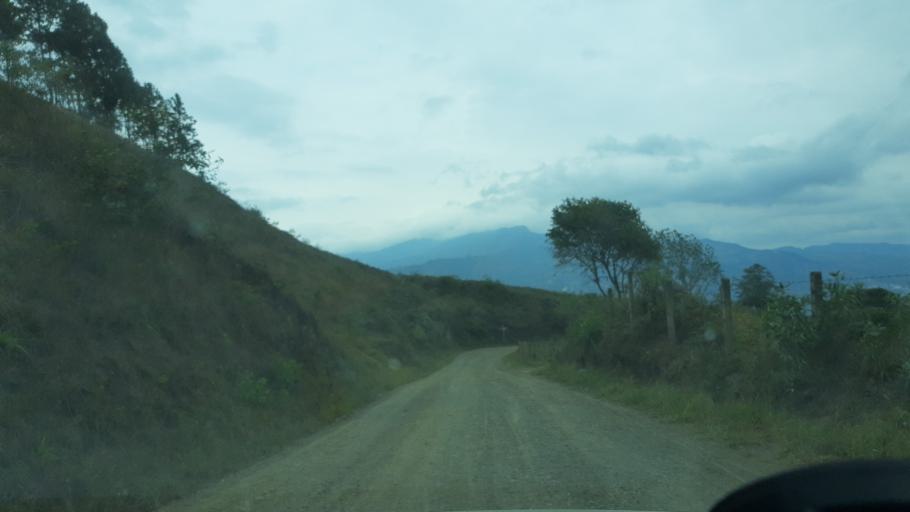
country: CO
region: Boyaca
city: Somondoco
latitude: 4.9812
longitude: -73.3771
